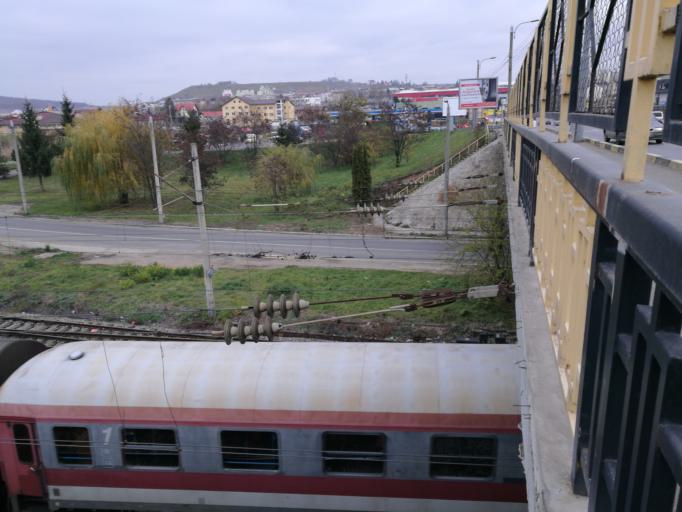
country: RO
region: Suceava
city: Suceava
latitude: 47.6677
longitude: 26.2727
